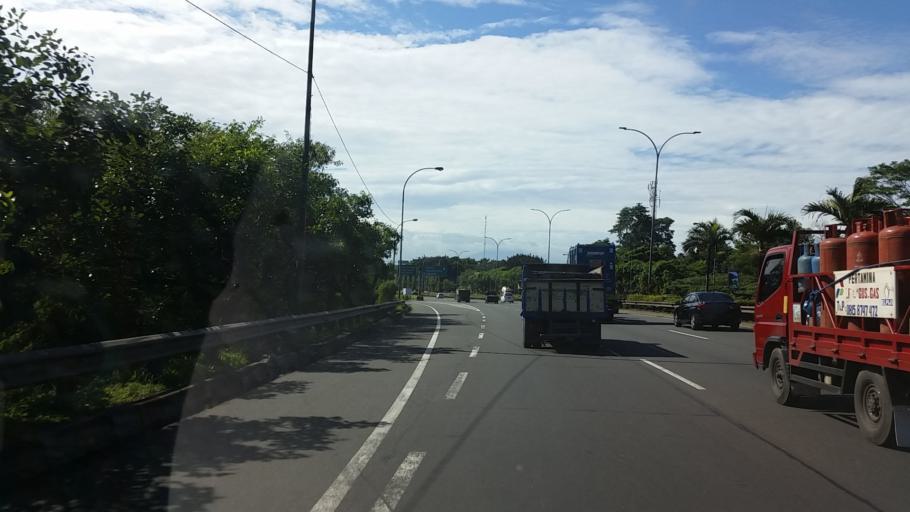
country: ID
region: Banten
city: South Tangerang
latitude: -6.2731
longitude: 106.7679
